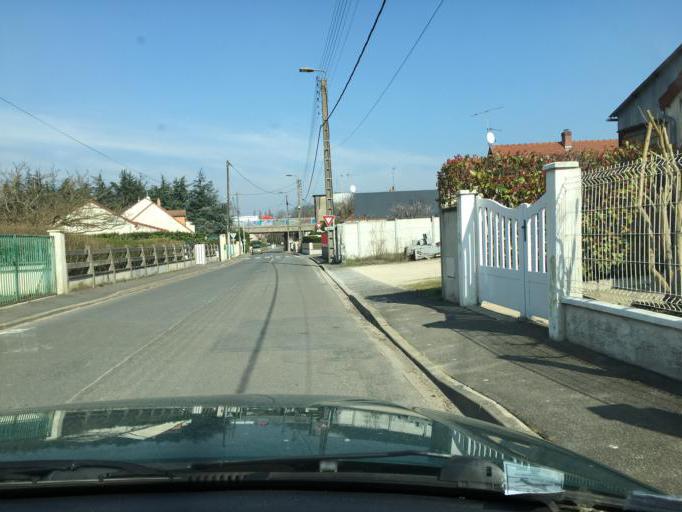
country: FR
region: Centre
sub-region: Departement du Loiret
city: Fleury-les-Aubrais
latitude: 47.9440
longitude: 1.9022
